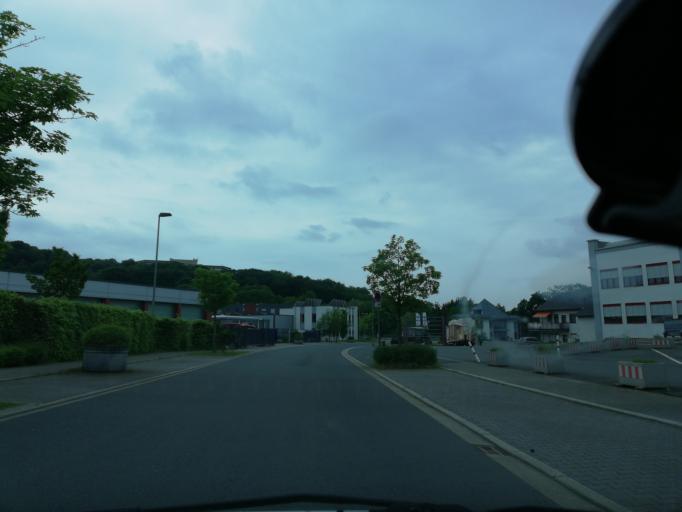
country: DE
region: North Rhine-Westphalia
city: Wetter (Ruhr)
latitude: 51.3816
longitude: 7.3877
